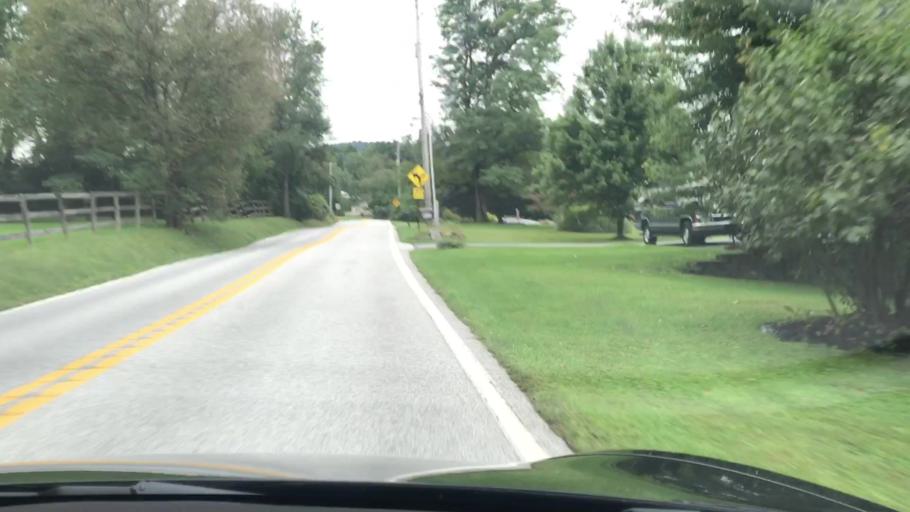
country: US
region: Pennsylvania
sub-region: York County
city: Dillsburg
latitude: 40.1210
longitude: -76.9591
